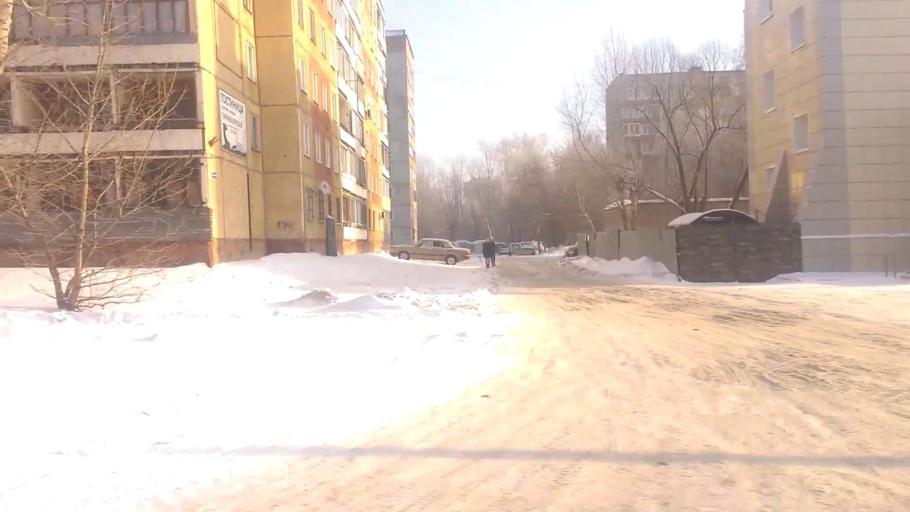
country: RU
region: Altai Krai
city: Novosilikatnyy
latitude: 53.3719
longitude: 83.6627
